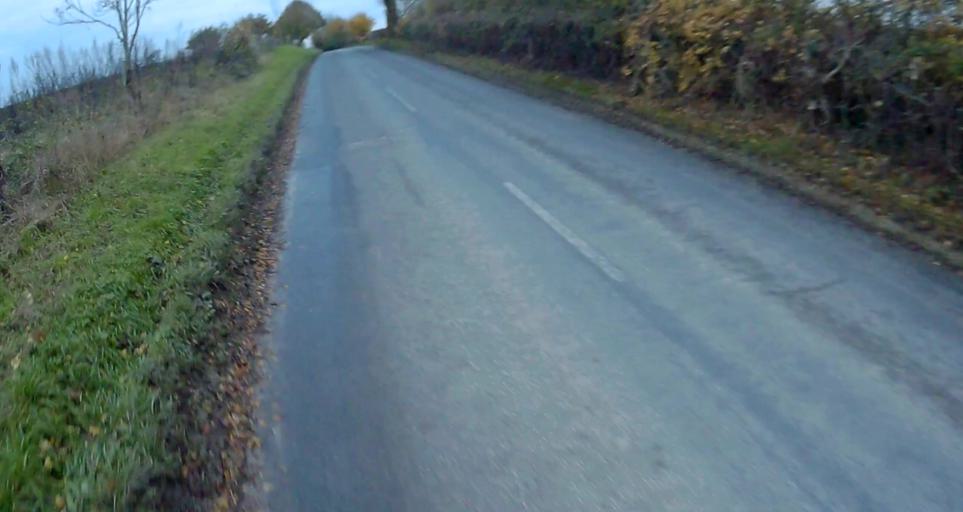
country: GB
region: England
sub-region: Hampshire
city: Odiham
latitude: 51.2516
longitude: -0.9636
